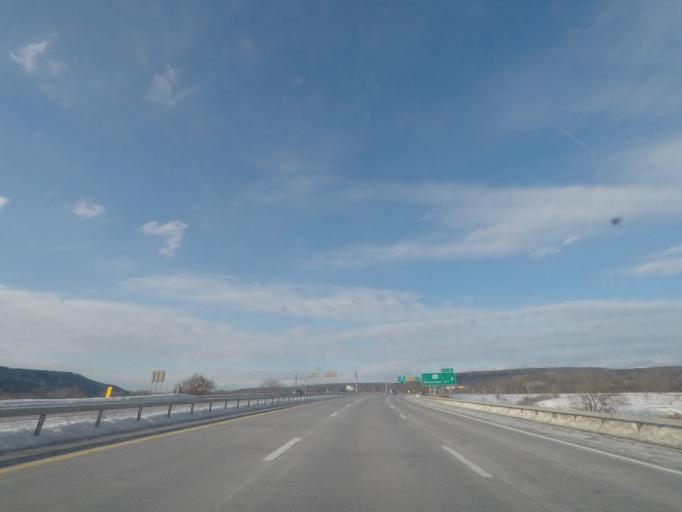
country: US
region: New York
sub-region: Schenectady County
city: Scotia
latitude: 42.8438
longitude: -74.0058
